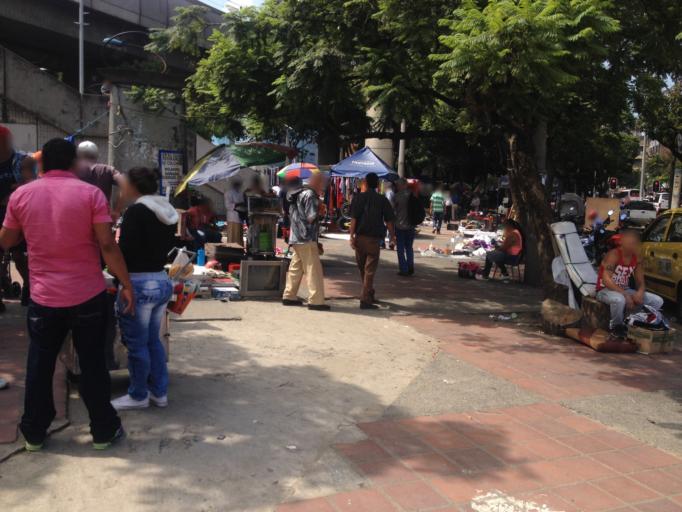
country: CO
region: Antioquia
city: Medellin
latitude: 6.2559
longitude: -75.5668
